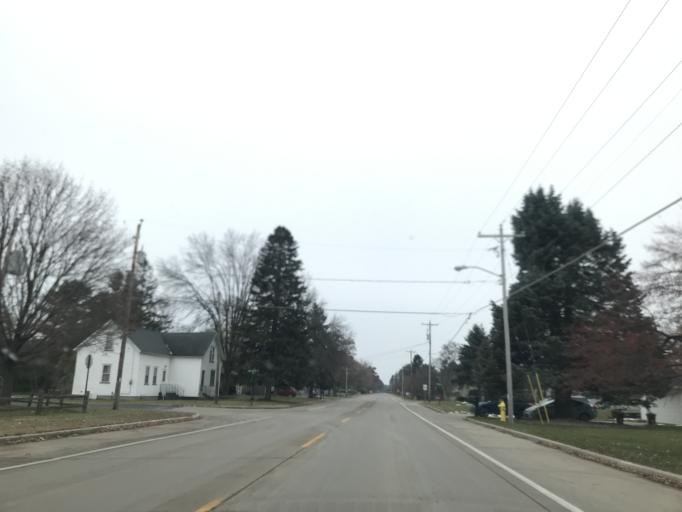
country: US
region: Wisconsin
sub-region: Marinette County
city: Marinette
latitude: 45.0767
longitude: -87.6194
